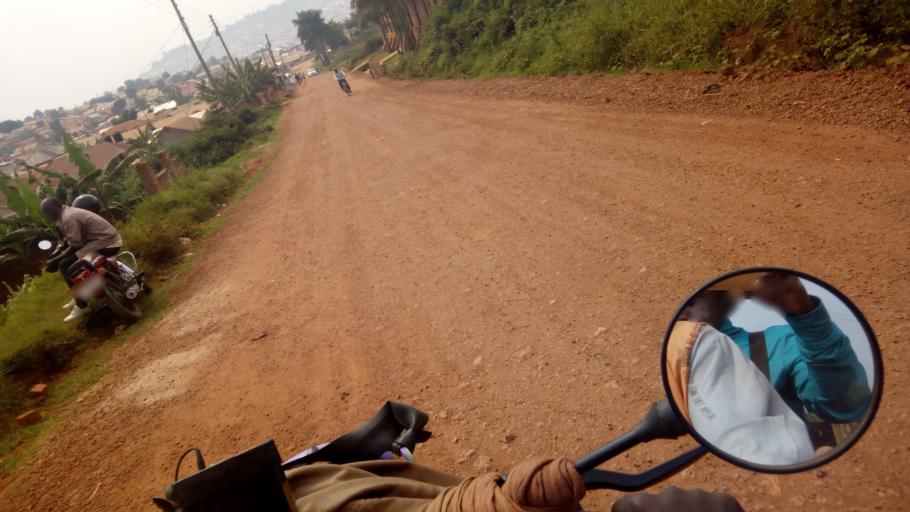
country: UG
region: Central Region
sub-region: Wakiso District
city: Kireka
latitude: 0.3161
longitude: 32.6536
